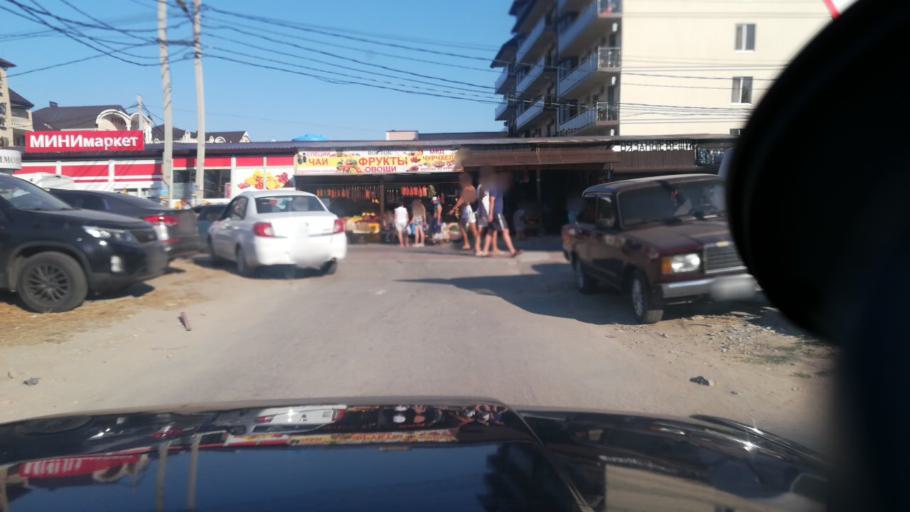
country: RU
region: Krasnodarskiy
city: Vityazevo
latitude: 44.9872
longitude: 37.2507
